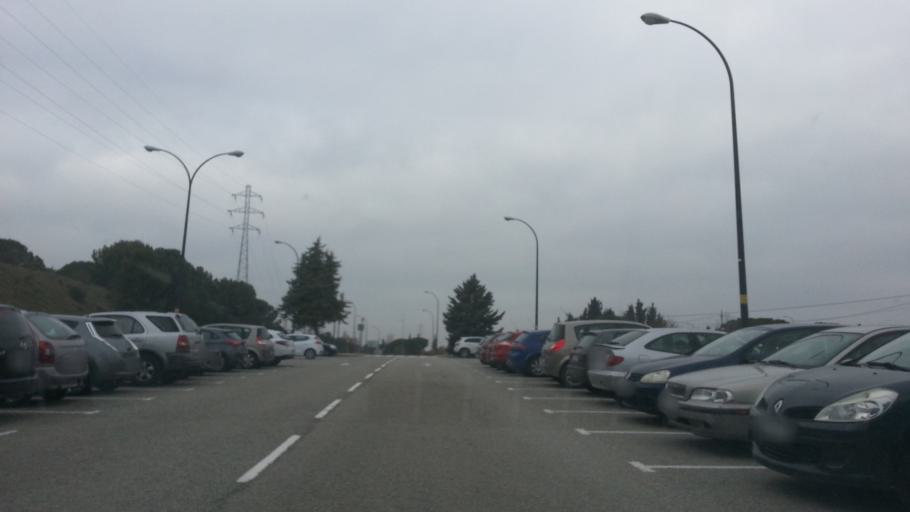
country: ES
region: Catalonia
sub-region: Provincia de Barcelona
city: Barbera del Valles
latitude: 41.5068
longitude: 2.1040
